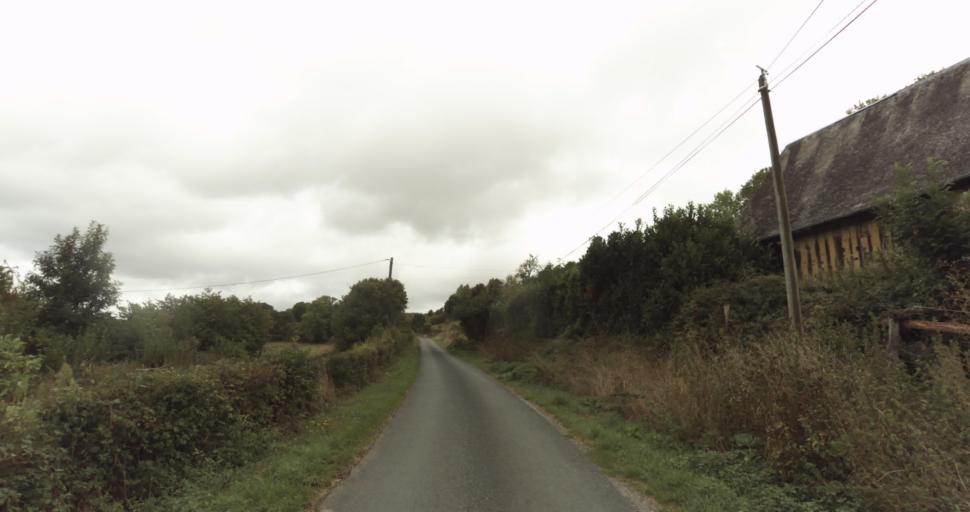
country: FR
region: Lower Normandy
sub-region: Departement de l'Orne
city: Gace
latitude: 48.8242
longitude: 0.2579
